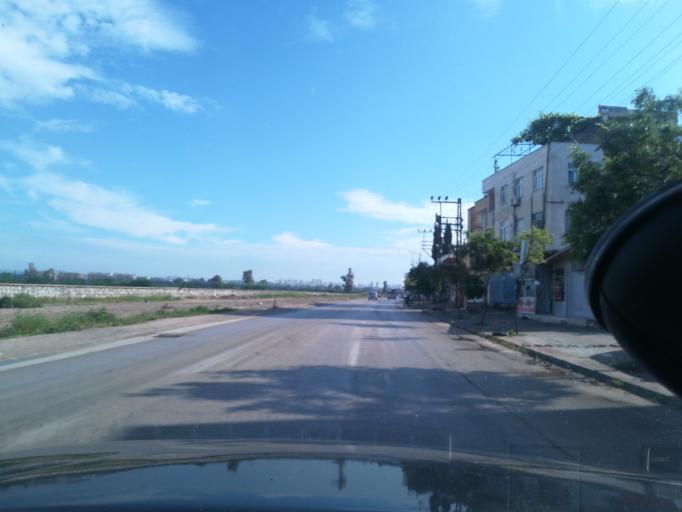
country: TR
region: Adana
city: Adana
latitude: 37.0104
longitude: 35.3580
